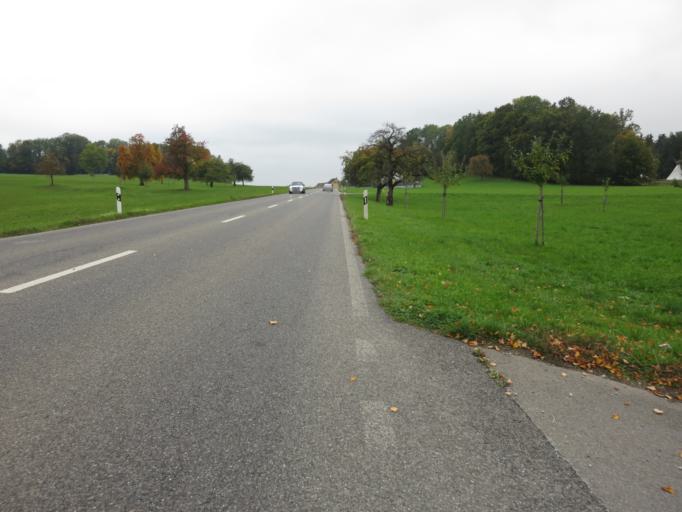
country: CH
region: Zurich
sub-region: Bezirk Hinwil
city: Bubikon
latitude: 47.2785
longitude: 8.8133
